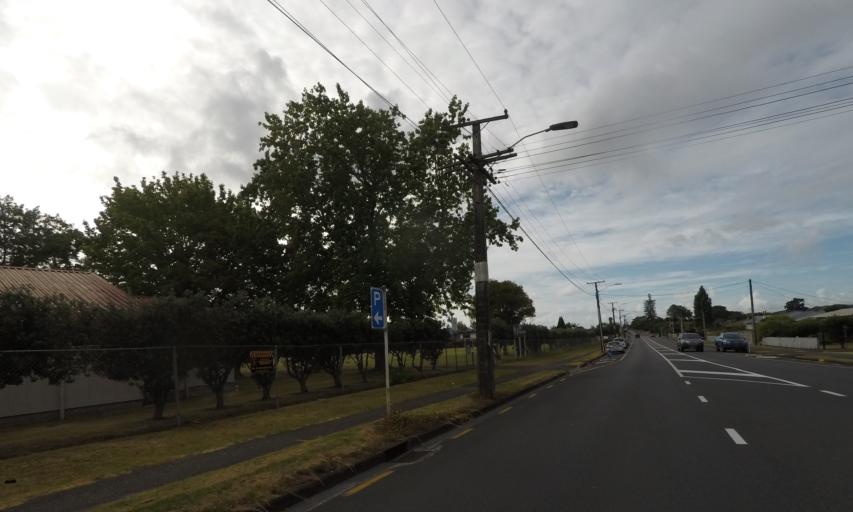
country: NZ
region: Northland
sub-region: Whangarei
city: Whangarei
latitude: -35.6854
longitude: 174.3021
